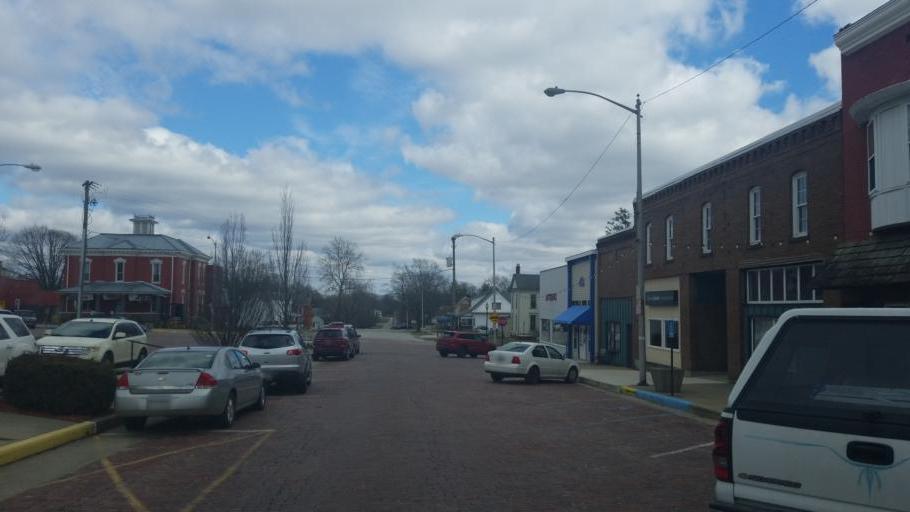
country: US
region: Indiana
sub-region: Parke County
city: Rockville
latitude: 39.7614
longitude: -87.2285
